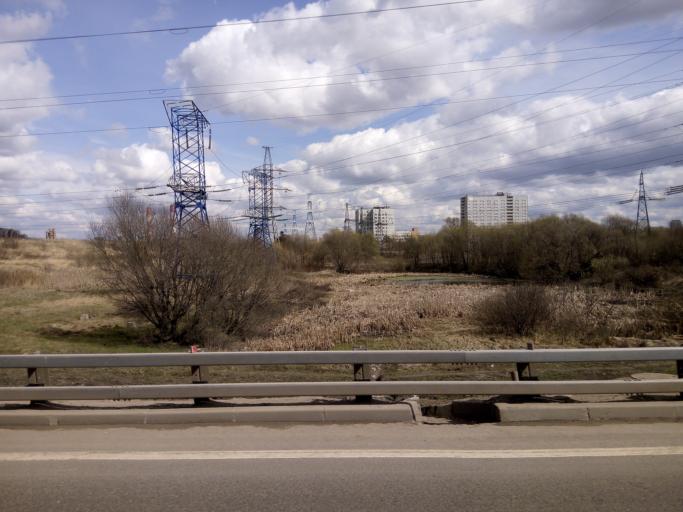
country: RU
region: Moscow
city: Mikhalkovo
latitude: 55.6866
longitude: 37.4157
